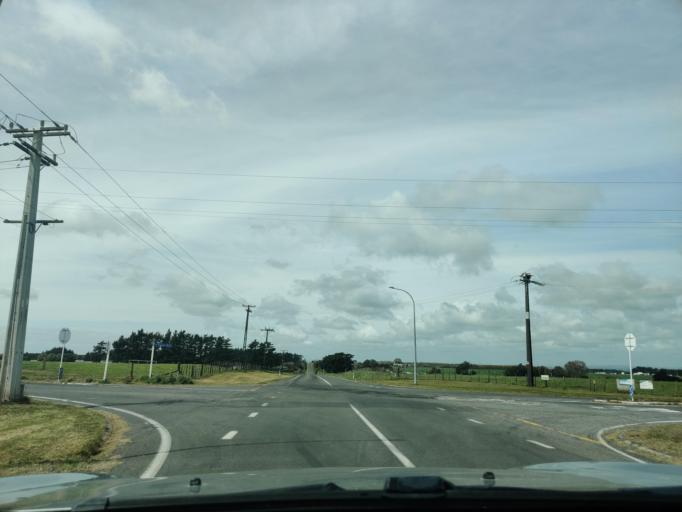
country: NZ
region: Taranaki
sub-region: South Taranaki District
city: Eltham
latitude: -39.4275
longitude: 174.1694
